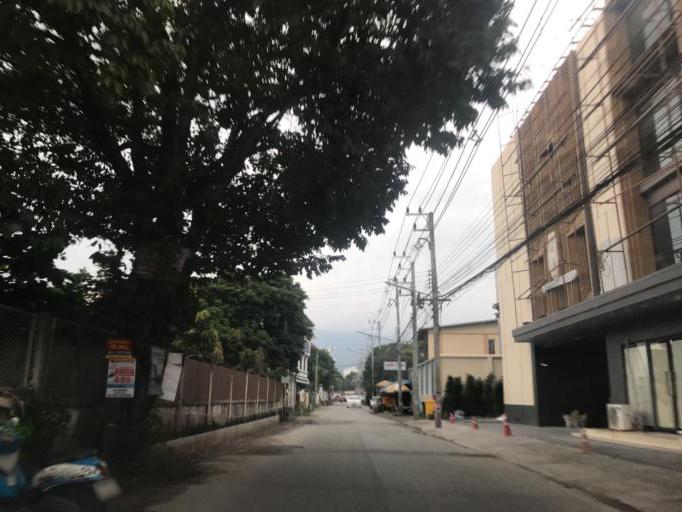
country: TH
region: Chiang Mai
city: Chiang Mai
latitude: 18.8056
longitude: 98.9737
